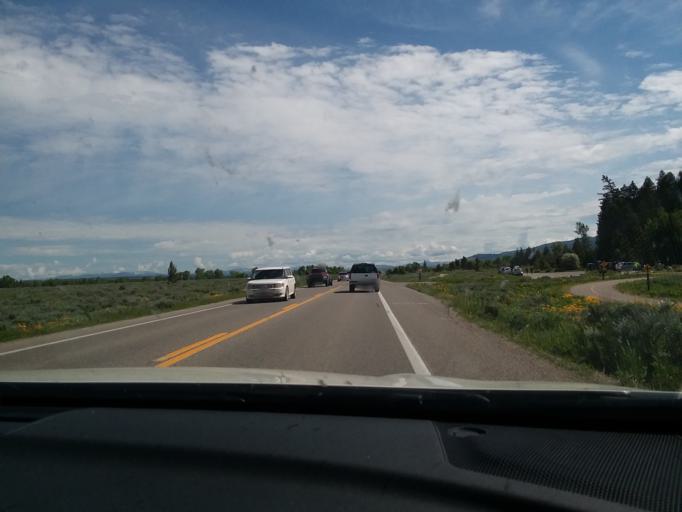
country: US
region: Wyoming
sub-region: Teton County
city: Jackson
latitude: 43.6610
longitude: -110.6999
